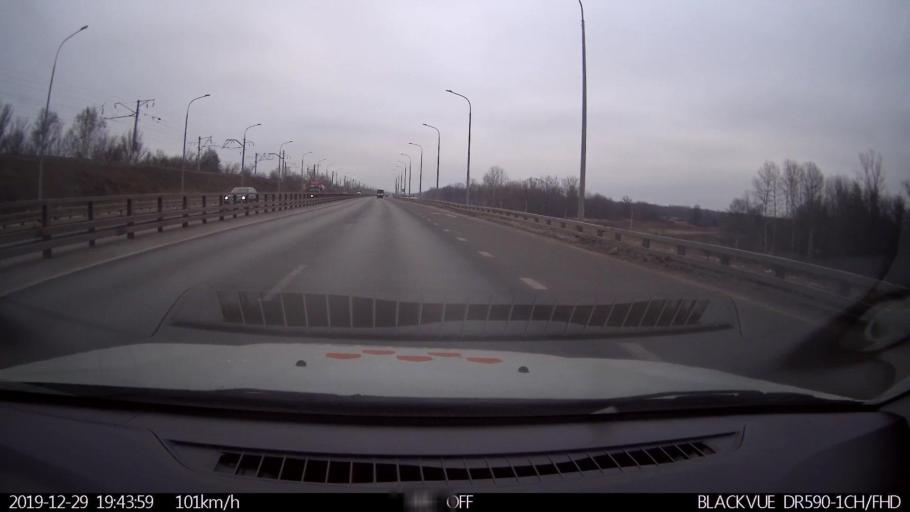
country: RU
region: Nizjnij Novgorod
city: Neklyudovo
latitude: 56.3695
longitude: 43.9429
